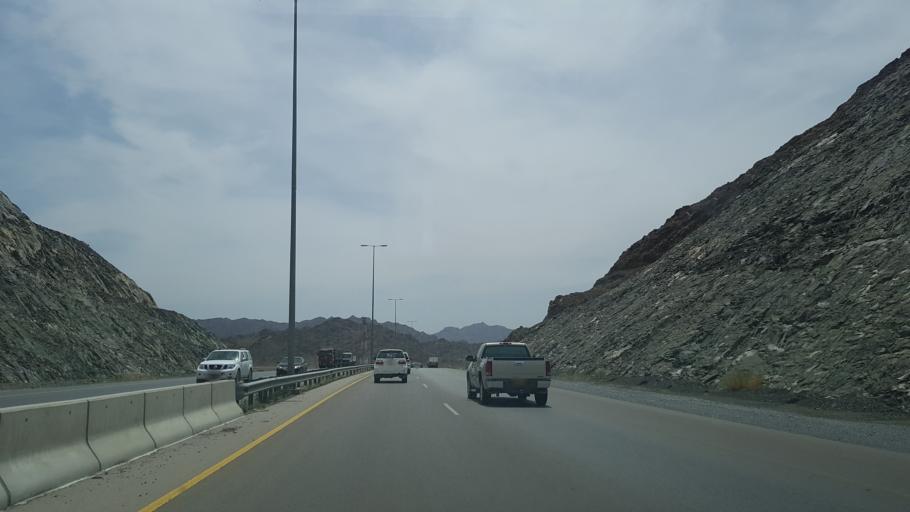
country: OM
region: Muhafazat ad Dakhiliyah
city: Izki
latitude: 22.9635
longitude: 57.7849
